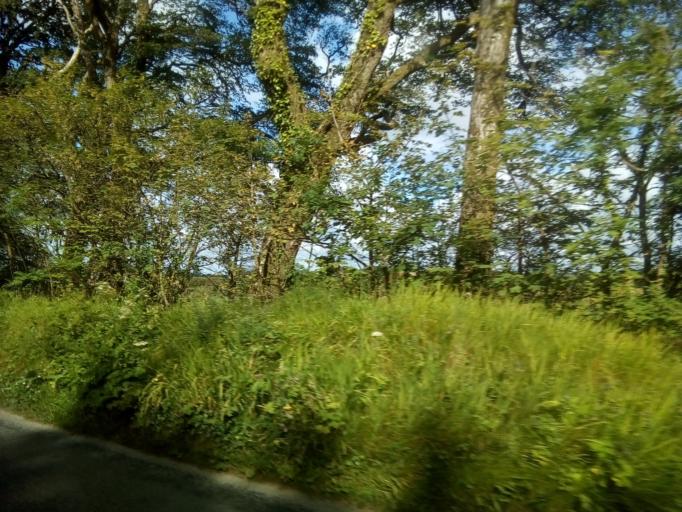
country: IE
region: Leinster
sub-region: Loch Garman
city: Loch Garman
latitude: 52.2749
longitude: -6.5447
